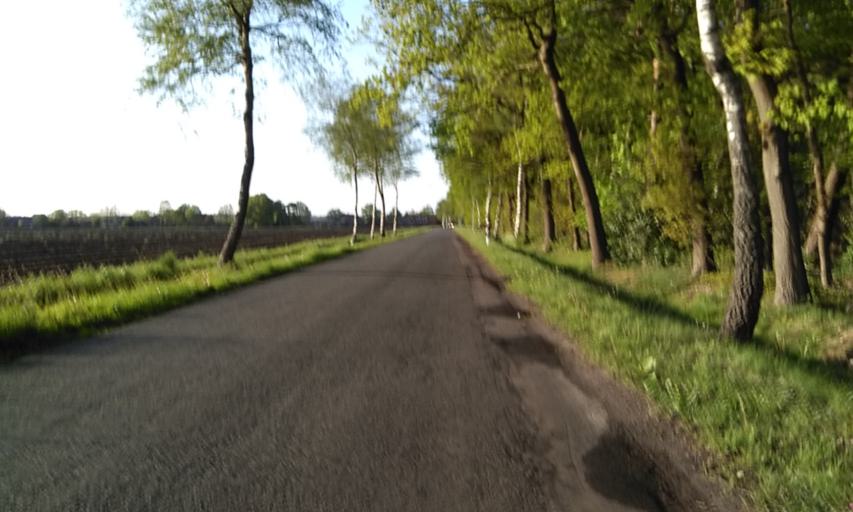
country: DE
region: Lower Saxony
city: Harsefeld
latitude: 53.4006
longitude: 9.5048
